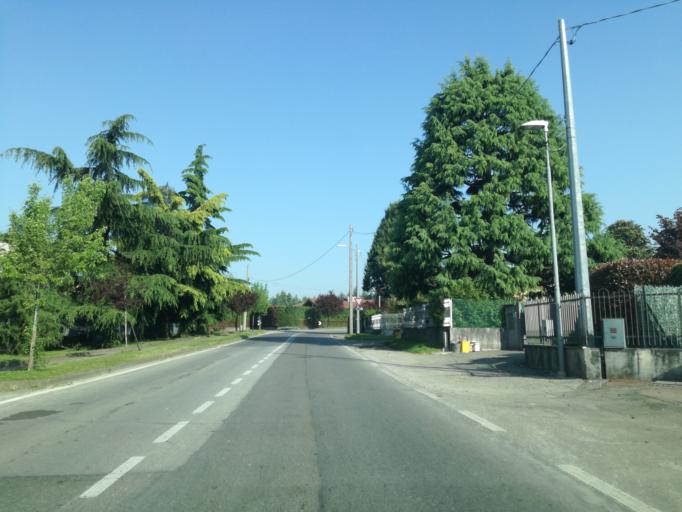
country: IT
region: Lombardy
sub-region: Provincia di Lecco
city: Merate
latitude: 45.6806
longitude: 9.4113
